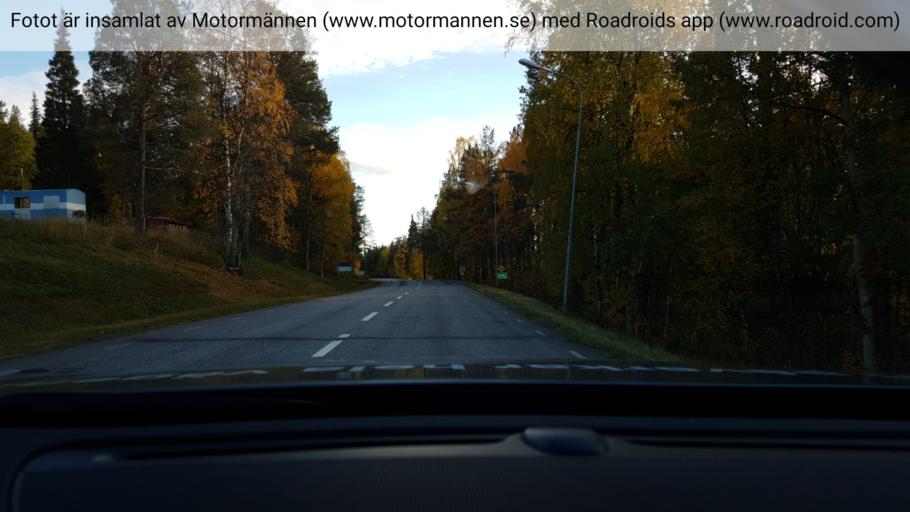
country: SE
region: Norrbotten
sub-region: Jokkmokks Kommun
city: Jokkmokk
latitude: 66.9489
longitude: 19.7967
